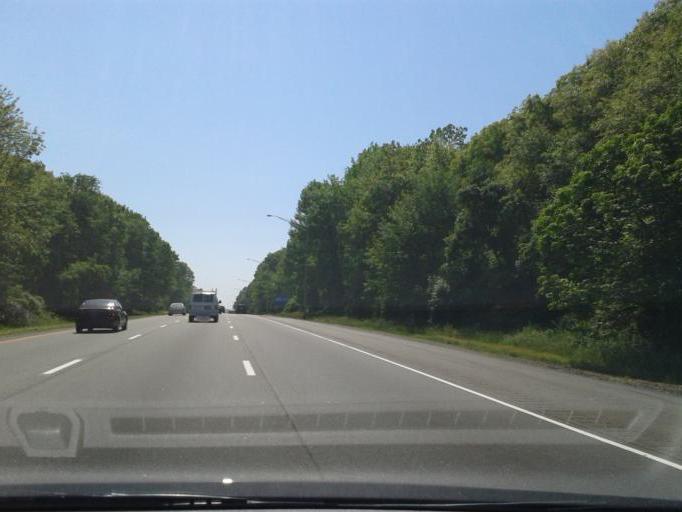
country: US
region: Connecticut
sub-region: New London County
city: Poquonock Bridge
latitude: 41.3709
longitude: -71.9993
